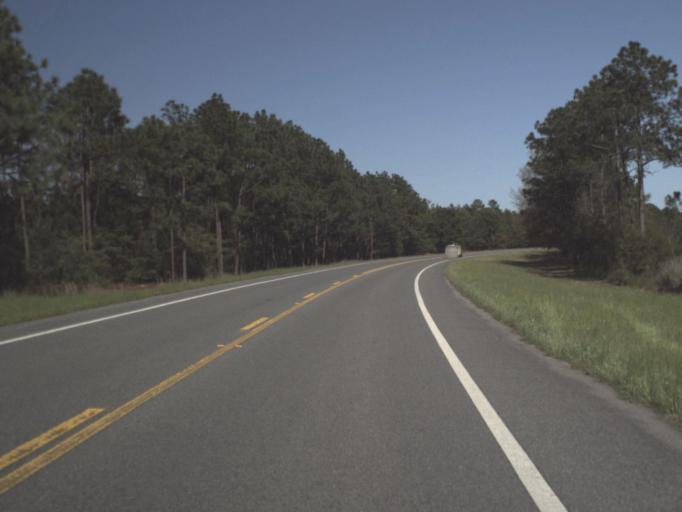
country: US
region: Florida
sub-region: Walton County
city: DeFuniak Springs
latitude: 30.7224
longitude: -86.0366
